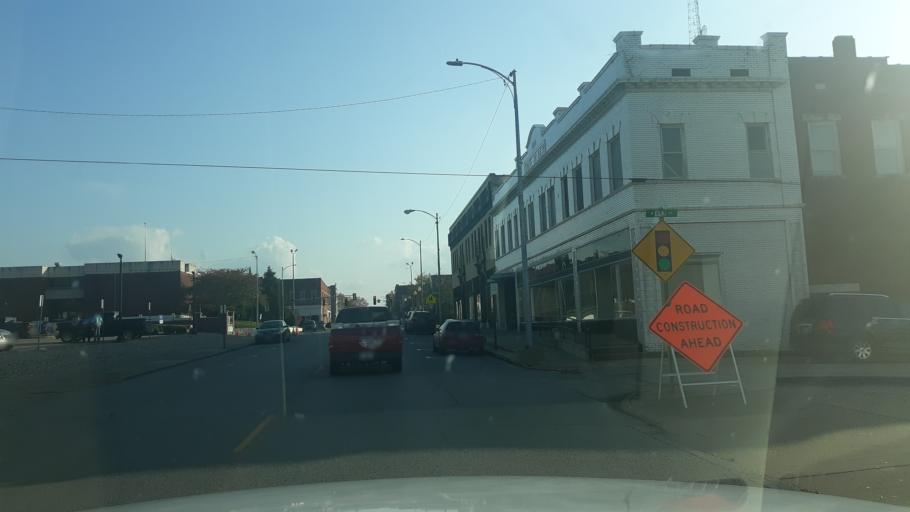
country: US
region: Illinois
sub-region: Saline County
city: Harrisburg
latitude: 37.7399
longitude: -88.5403
